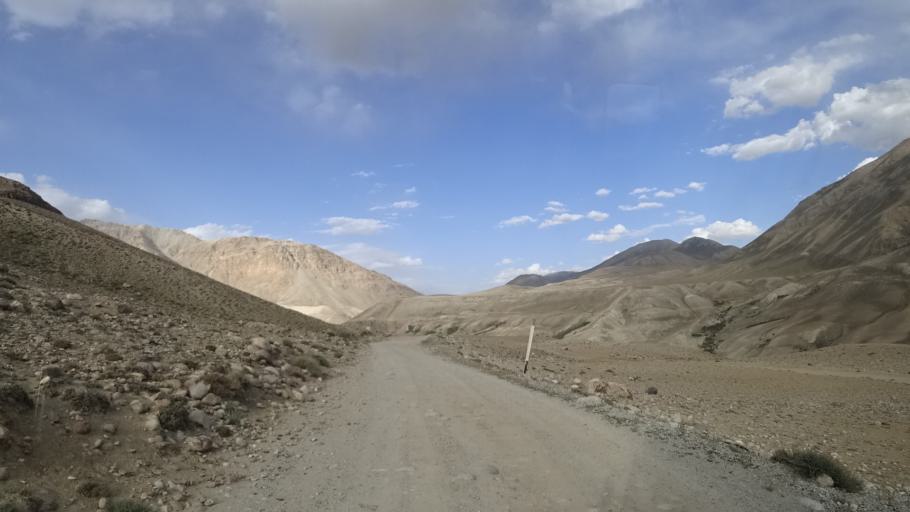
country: AF
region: Badakhshan
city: Khandud
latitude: 37.2227
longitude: 72.7952
